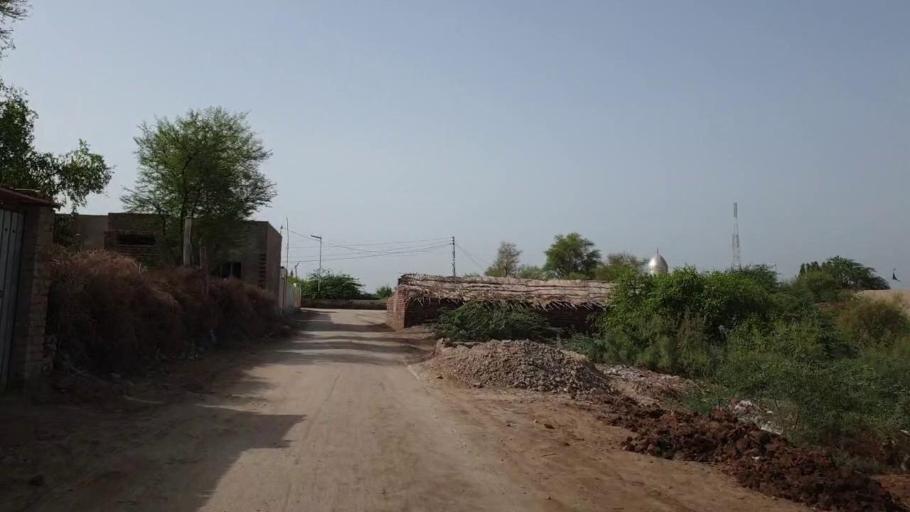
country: PK
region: Sindh
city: Jam Sahib
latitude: 26.2990
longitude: 68.6317
